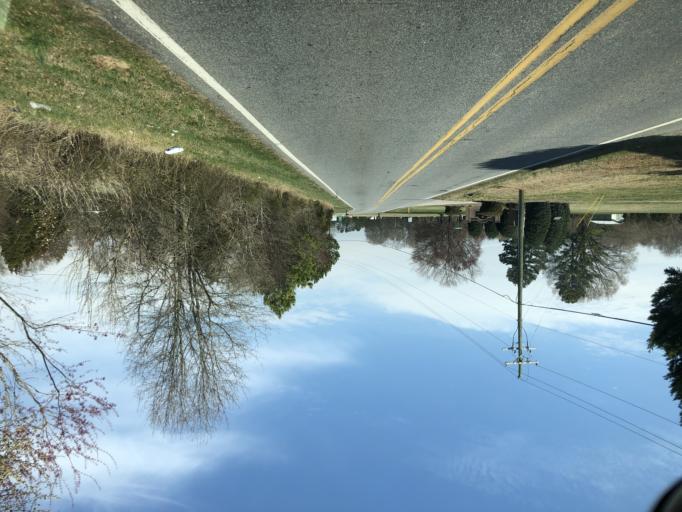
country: US
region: North Carolina
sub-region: Gaston County
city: Stanley
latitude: 35.3402
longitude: -81.0924
